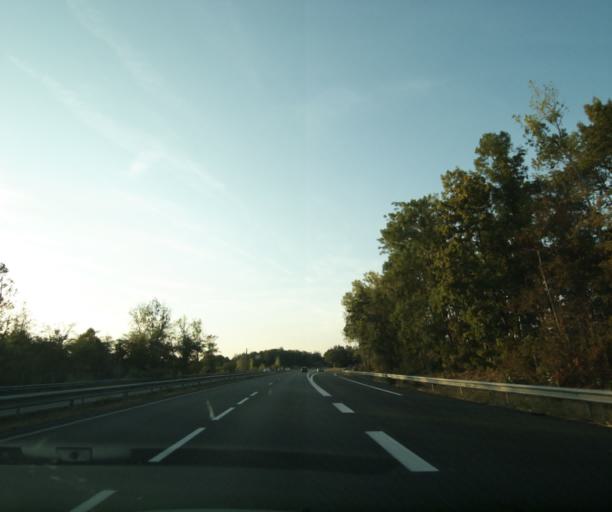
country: FR
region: Aquitaine
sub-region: Departement du Lot-et-Garonne
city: Estillac
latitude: 44.1676
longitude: 0.5820
